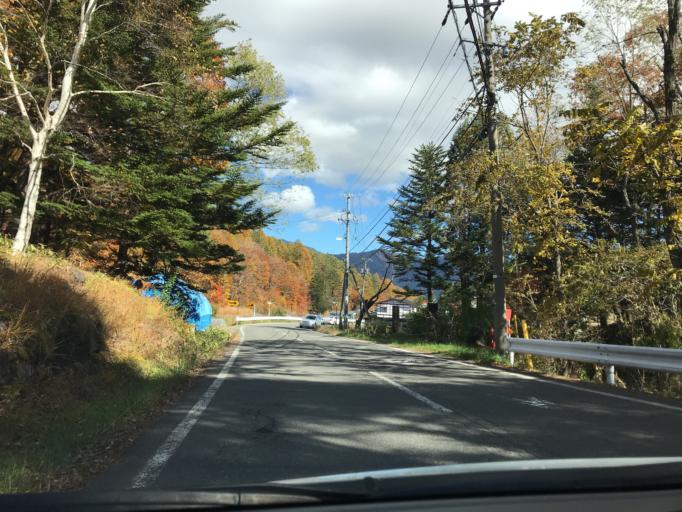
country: JP
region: Nagano
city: Toyoshina
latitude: 36.1242
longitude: 137.6458
